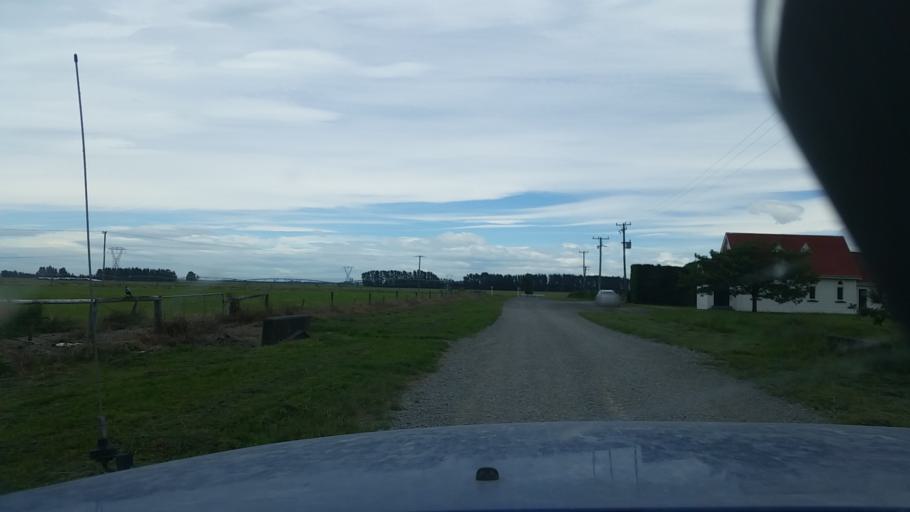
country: NZ
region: Canterbury
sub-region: Ashburton District
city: Tinwald
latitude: -43.8496
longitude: 171.6439
